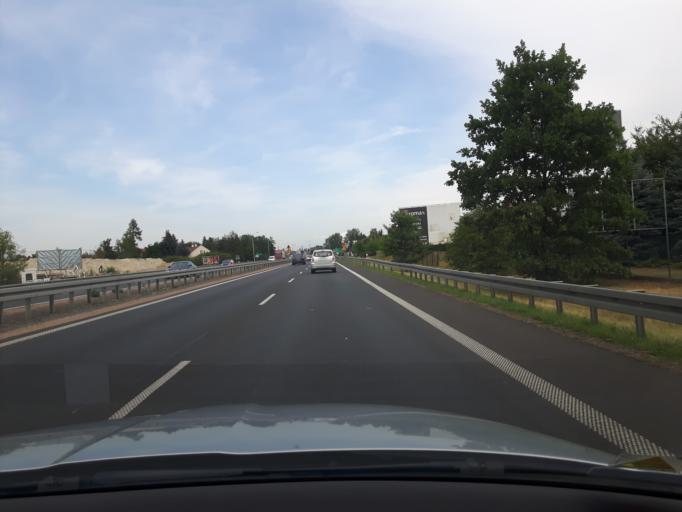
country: PL
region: Masovian Voivodeship
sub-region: Powiat warszawski zachodni
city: Kielpin
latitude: 52.3449
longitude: 20.8634
